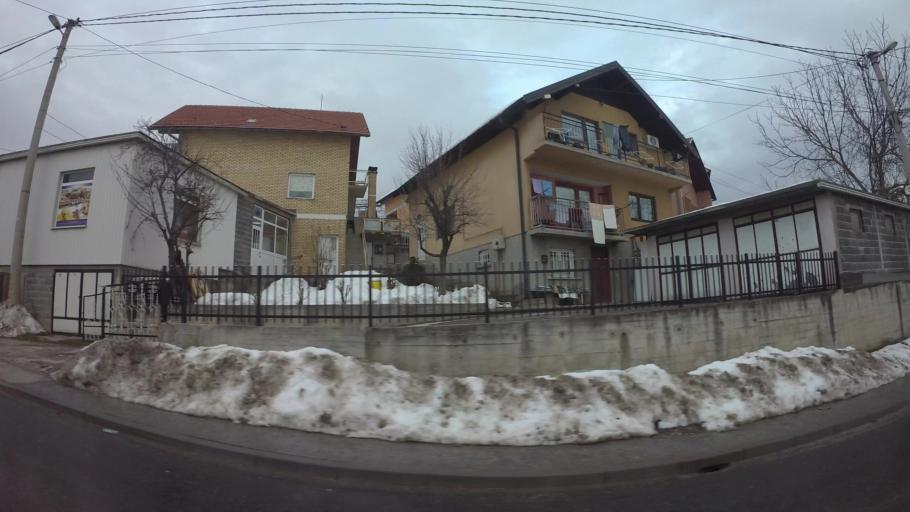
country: BA
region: Federation of Bosnia and Herzegovina
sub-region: Kanton Sarajevo
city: Sarajevo
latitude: 43.8582
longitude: 18.3537
